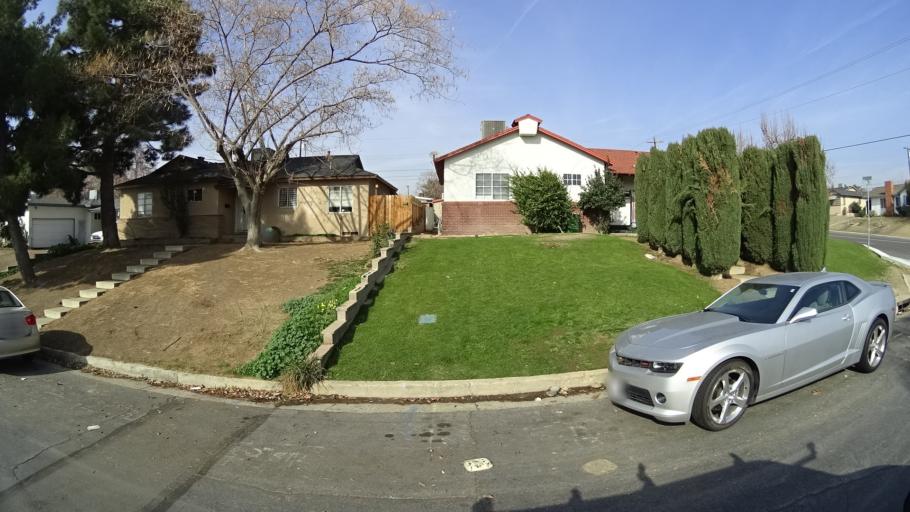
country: US
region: California
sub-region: Kern County
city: Oildale
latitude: 35.4022
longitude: -118.9767
